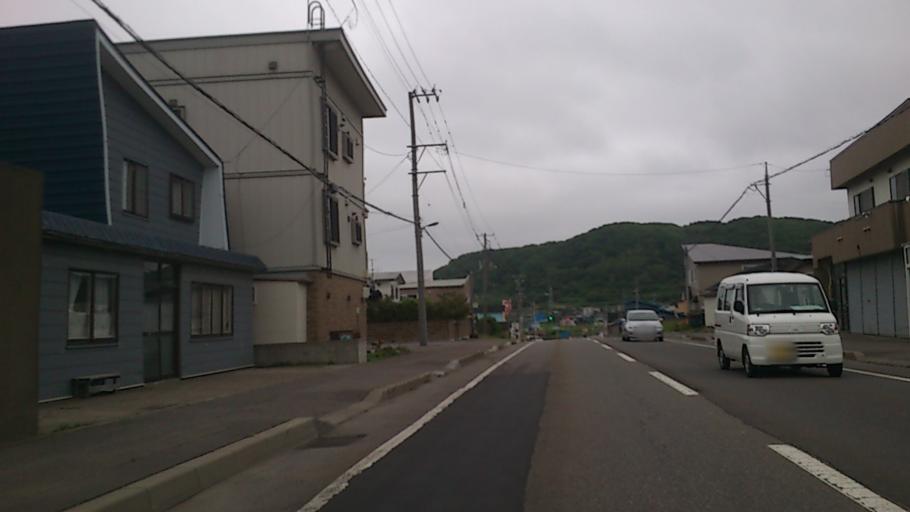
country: JP
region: Hokkaido
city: Kamiiso
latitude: 41.9760
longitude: 140.1364
